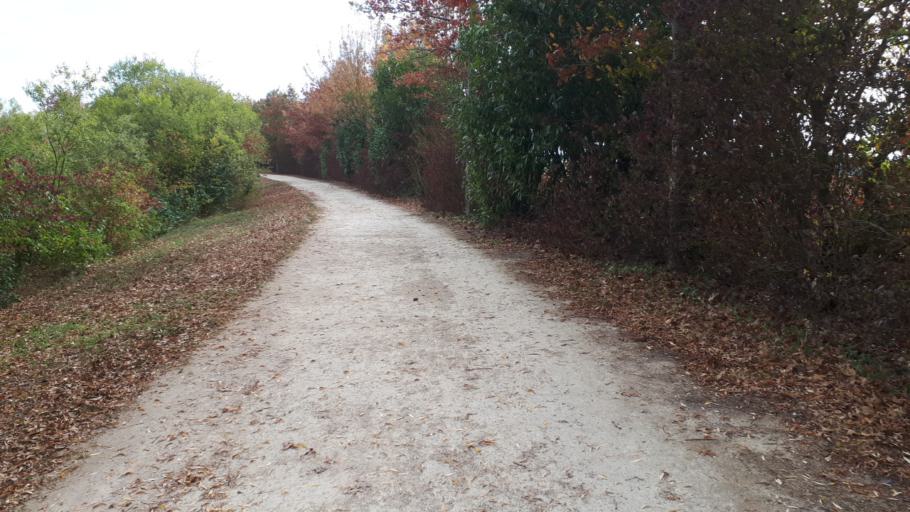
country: FR
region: Centre
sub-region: Departement du Loir-et-Cher
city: Villiers-sur-Loir
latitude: 47.7958
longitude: 0.9914
